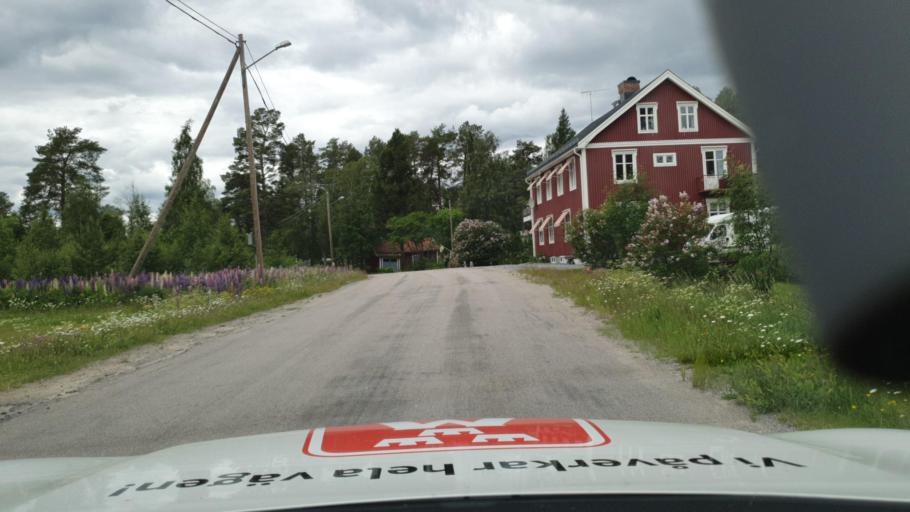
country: SE
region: Vaesterbotten
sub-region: Bjurholms Kommun
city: Bjurholm
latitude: 63.7855
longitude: 19.1832
